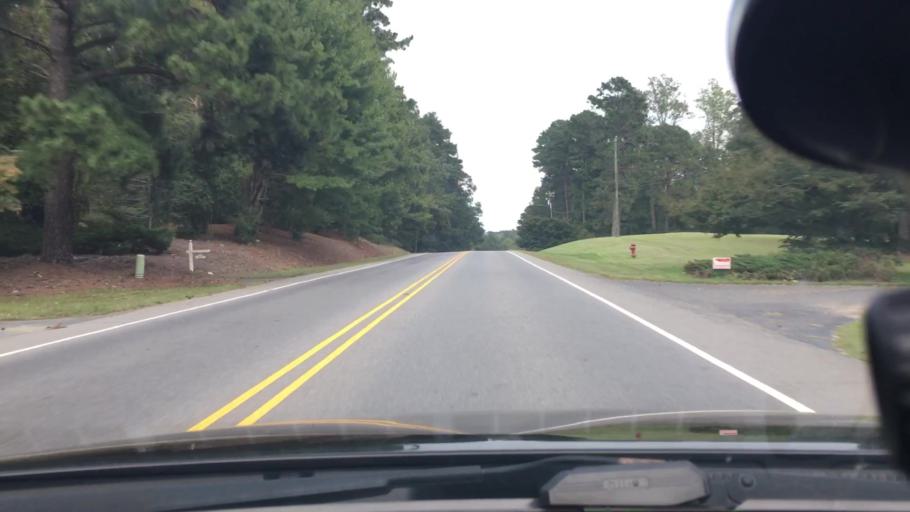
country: US
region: North Carolina
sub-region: Montgomery County
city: Troy
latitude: 35.3601
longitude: -79.8825
